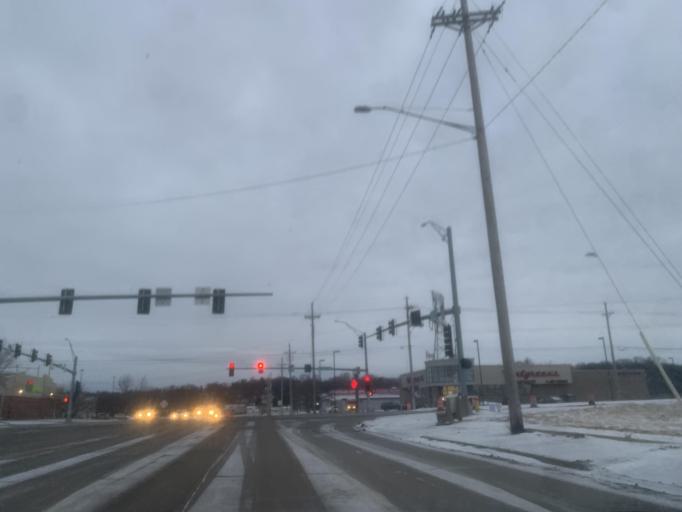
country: US
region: Nebraska
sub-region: Douglas County
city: Ralston
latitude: 41.2347
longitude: -96.0527
